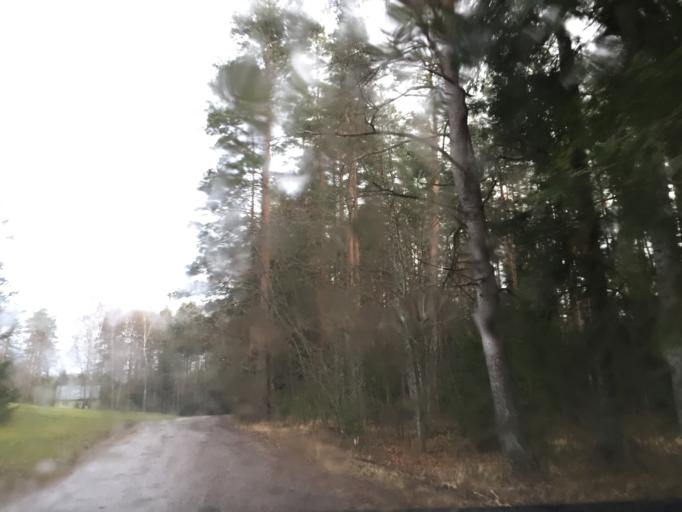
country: LV
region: Valmieras Rajons
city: Valmiera
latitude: 57.5481
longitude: 25.4689
